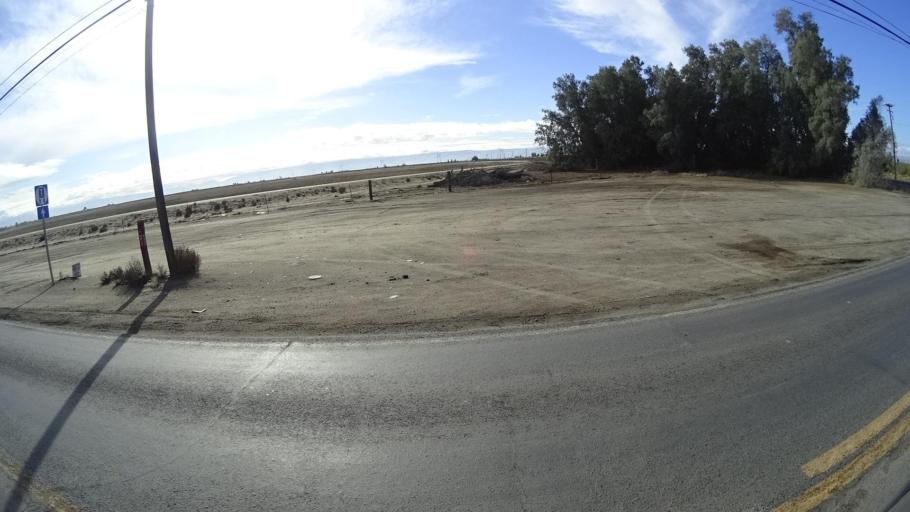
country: US
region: California
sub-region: Kern County
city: Rosedale
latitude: 35.3836
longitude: -119.2513
